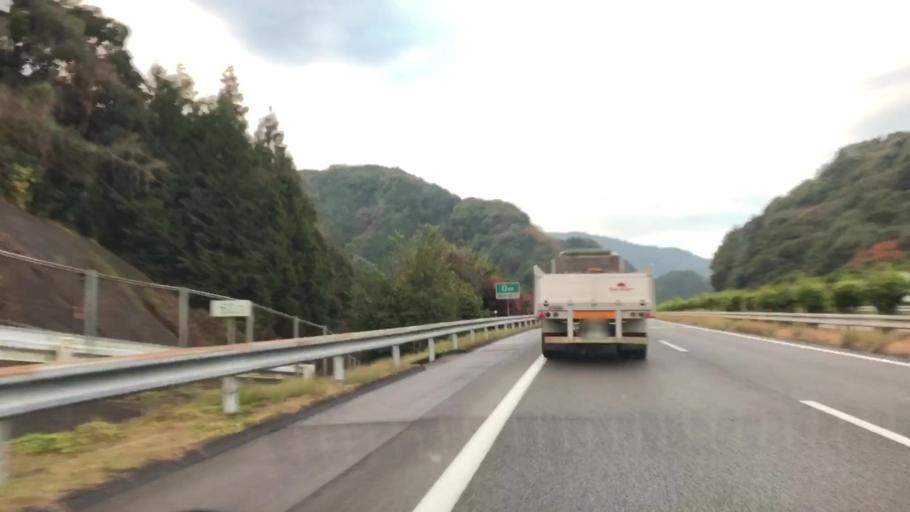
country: JP
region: Saga Prefecture
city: Takeocho-takeo
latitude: 33.1651
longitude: 130.0329
